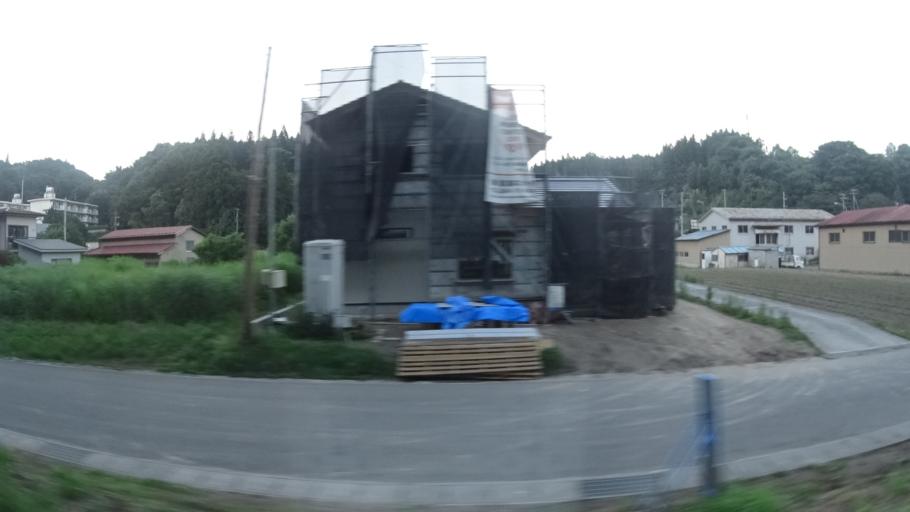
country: JP
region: Fukushima
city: Funehikimachi-funehiki
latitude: 37.2874
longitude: 140.6337
